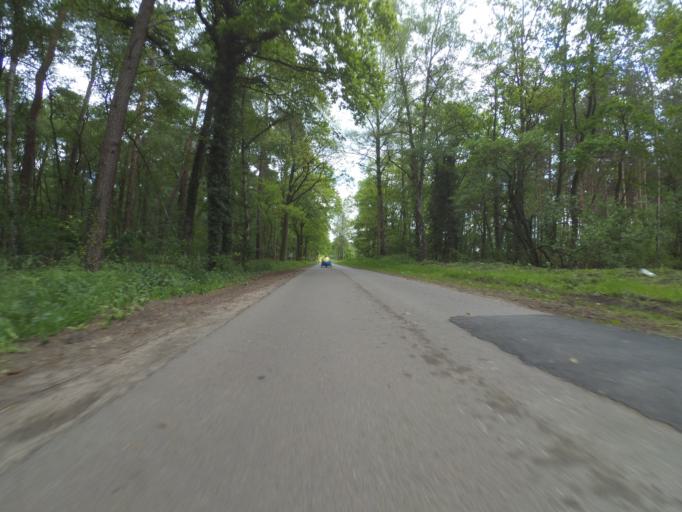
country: DE
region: Lower Saxony
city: Wietze
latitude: 52.5677
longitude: 9.8643
